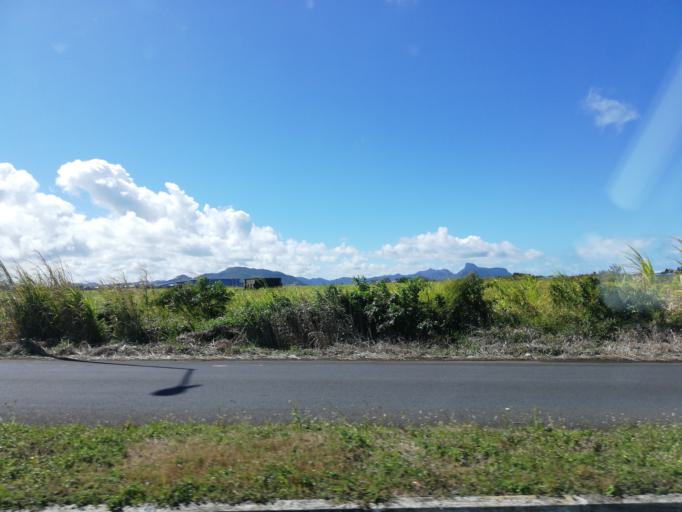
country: MU
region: Grand Port
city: Plaine Magnien
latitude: -20.4440
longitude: 57.6791
